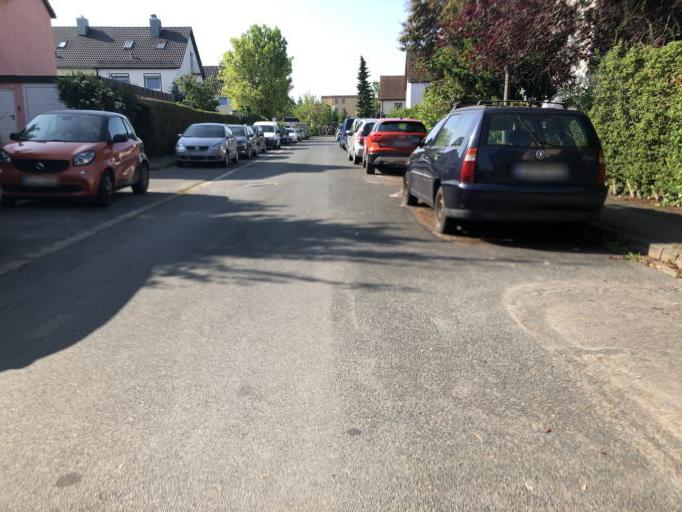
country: DE
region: Bavaria
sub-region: Regierungsbezirk Mittelfranken
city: Erlangen
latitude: 49.5546
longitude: 11.0209
